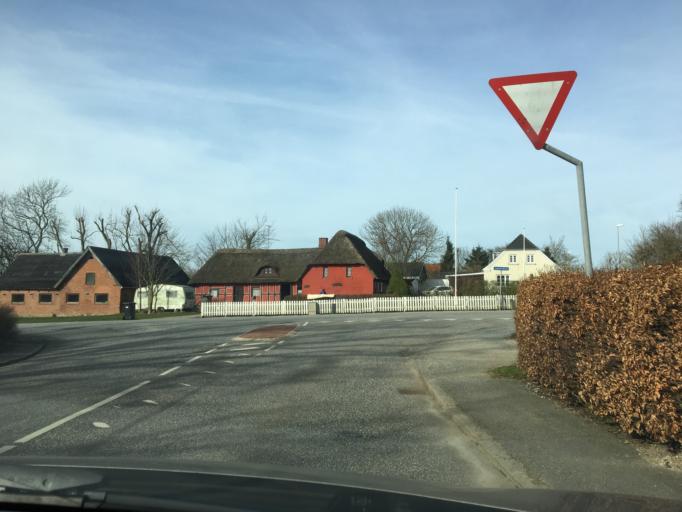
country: DK
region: Central Jutland
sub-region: Hedensted Kommune
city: Hedensted
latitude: 55.7333
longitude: 9.6610
